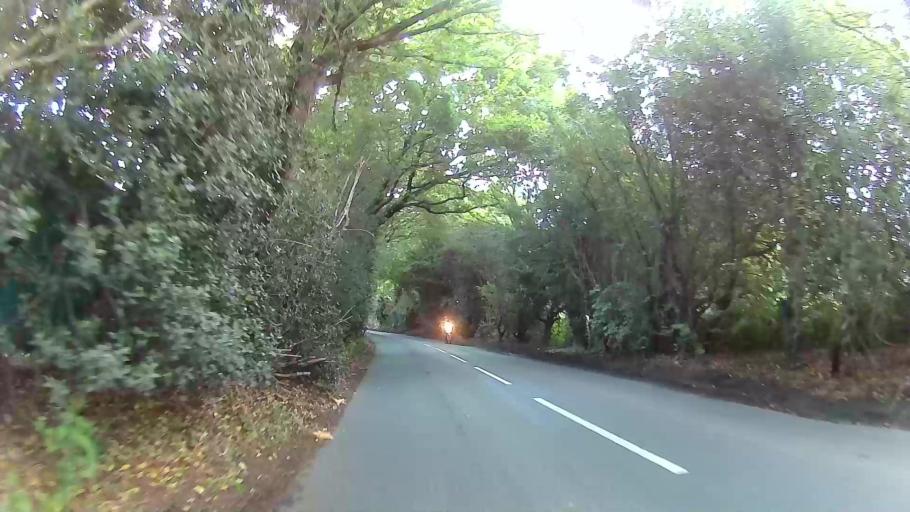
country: GB
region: England
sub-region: Greater London
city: Hainault
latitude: 51.6325
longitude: 0.1386
